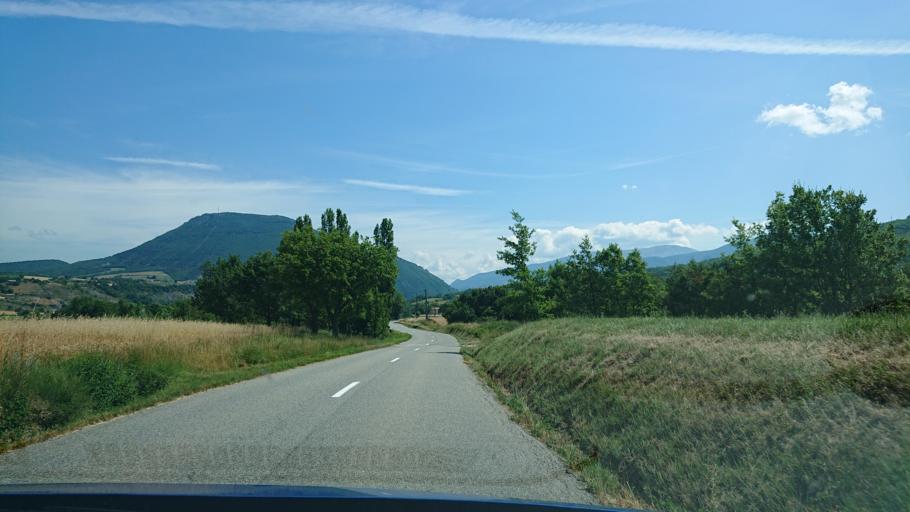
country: FR
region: Provence-Alpes-Cote d'Azur
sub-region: Departement des Alpes-de-Haute-Provence
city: Sisteron
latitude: 44.2489
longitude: 5.9541
